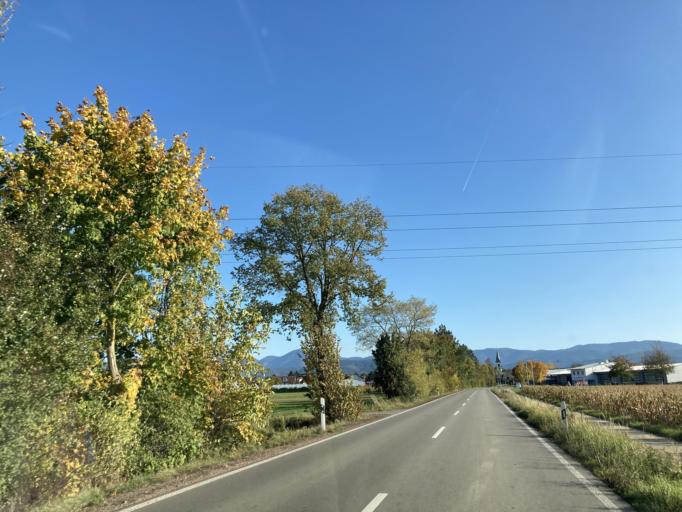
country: DE
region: Baden-Wuerttemberg
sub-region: Freiburg Region
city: Eschbach
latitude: 47.8948
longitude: 7.6474
